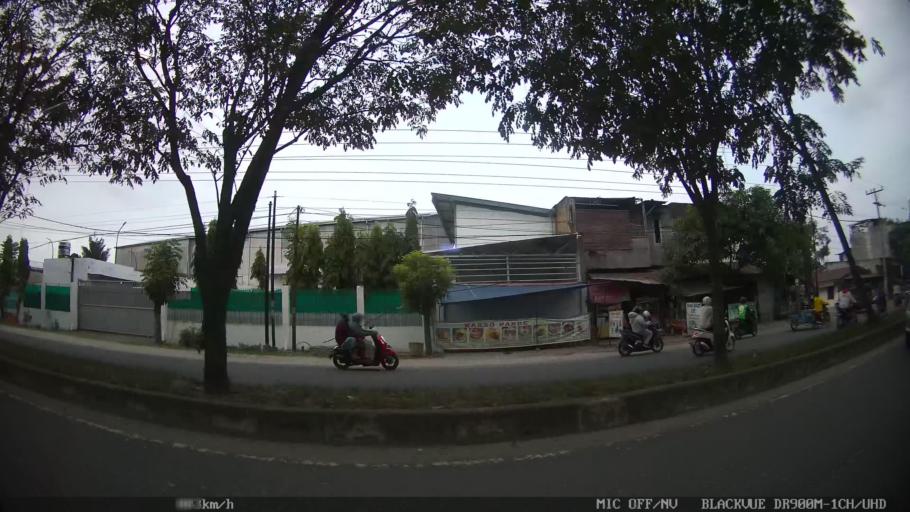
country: ID
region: North Sumatra
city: Sunggal
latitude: 3.5633
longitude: 98.6162
